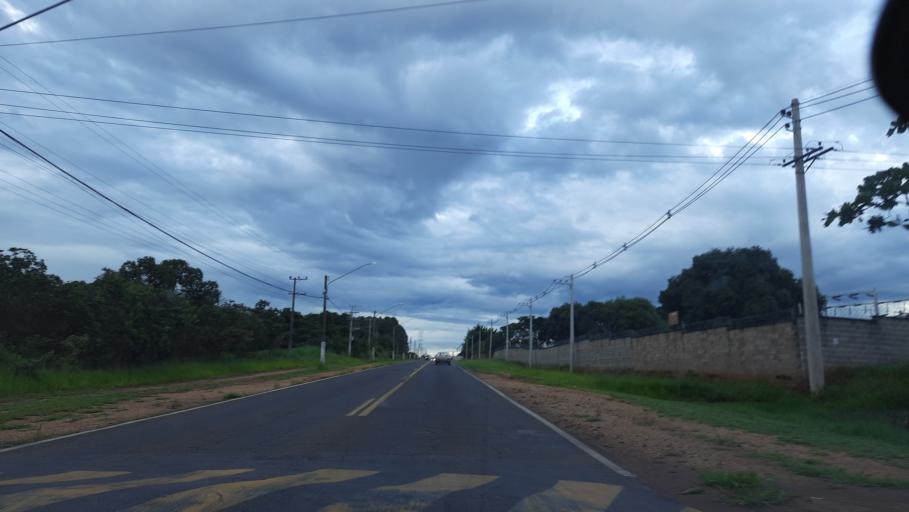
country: BR
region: Sao Paulo
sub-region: Casa Branca
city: Casa Branca
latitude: -21.7749
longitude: -47.0705
